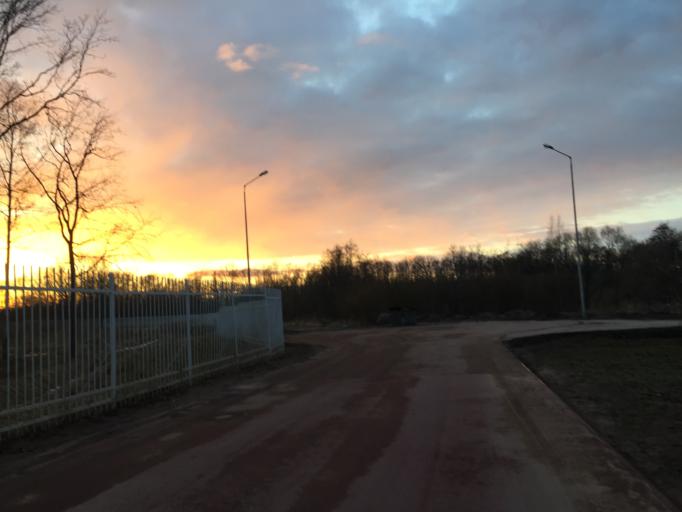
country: RU
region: St.-Petersburg
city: Pushkin
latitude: 59.7262
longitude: 30.3778
